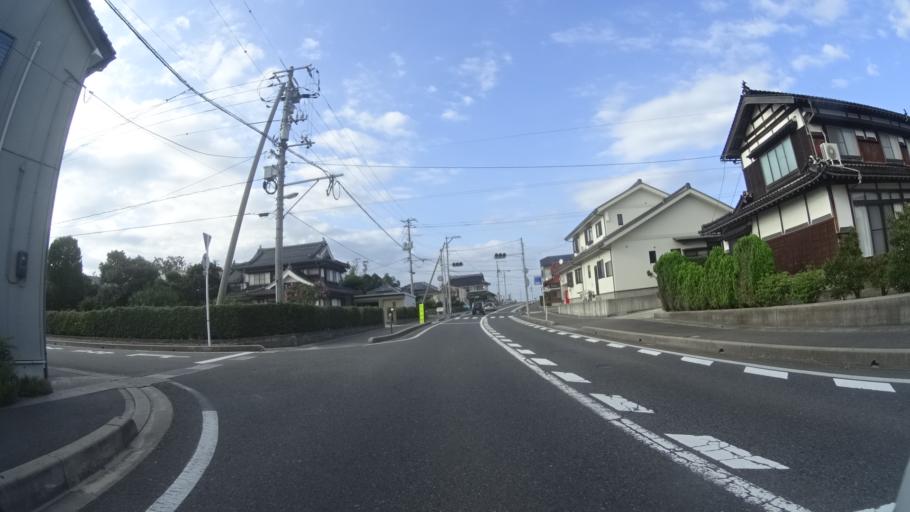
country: JP
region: Tottori
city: Kurayoshi
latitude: 35.4903
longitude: 133.8639
